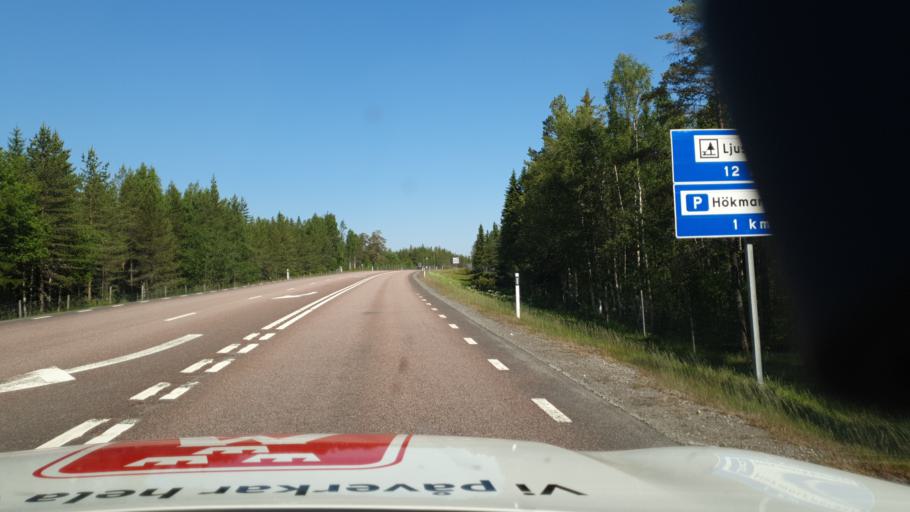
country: SE
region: Vaesterbotten
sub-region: Skelleftea Kommun
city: Burea
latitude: 64.4326
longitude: 21.2806
